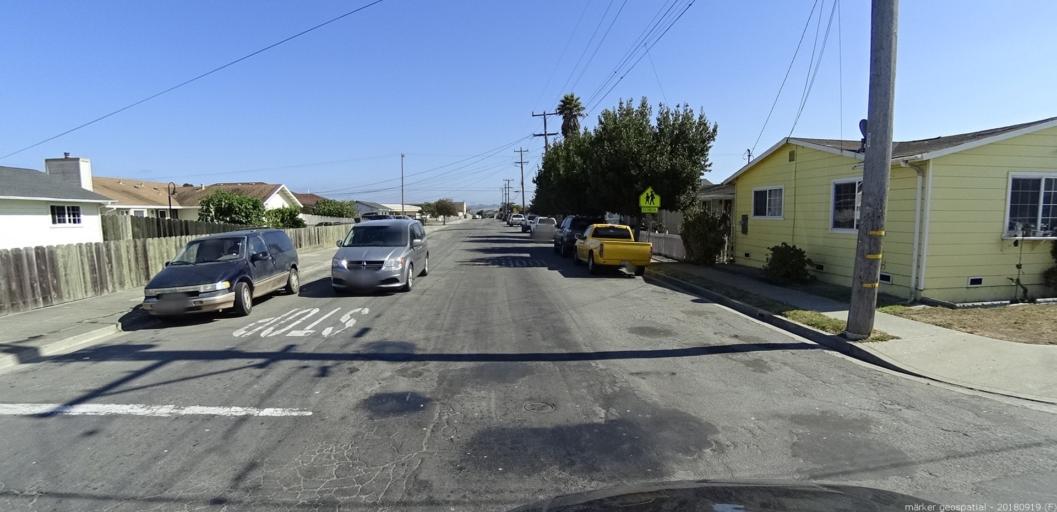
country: US
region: California
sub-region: Monterey County
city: Castroville
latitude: 36.7702
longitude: -121.7586
